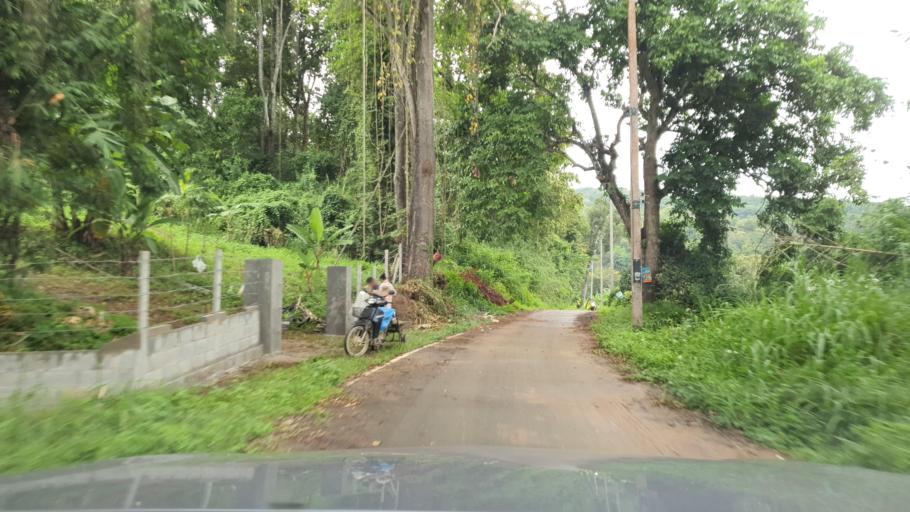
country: TH
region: Chiang Mai
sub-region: Amphoe Chiang Dao
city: Chiang Dao
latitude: 19.3350
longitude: 98.9280
